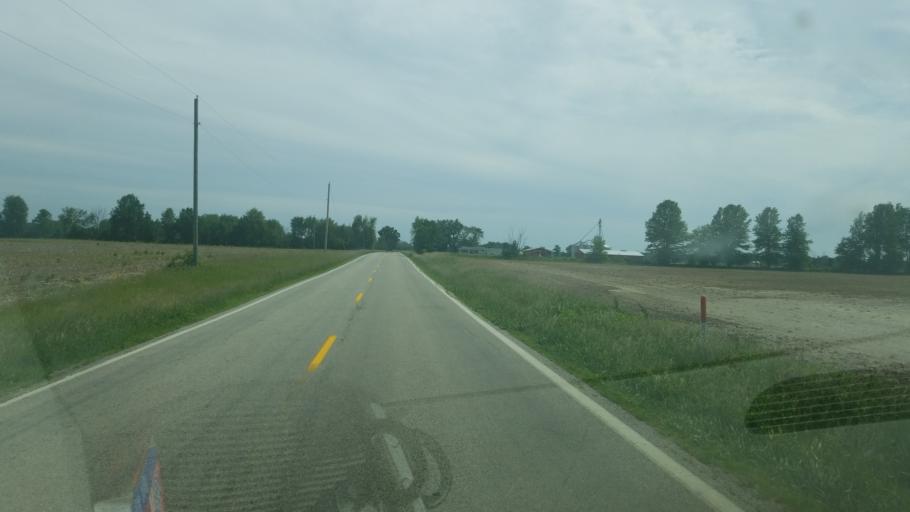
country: US
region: Ohio
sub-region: Delaware County
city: Ashley
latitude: 40.4660
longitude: -82.9631
